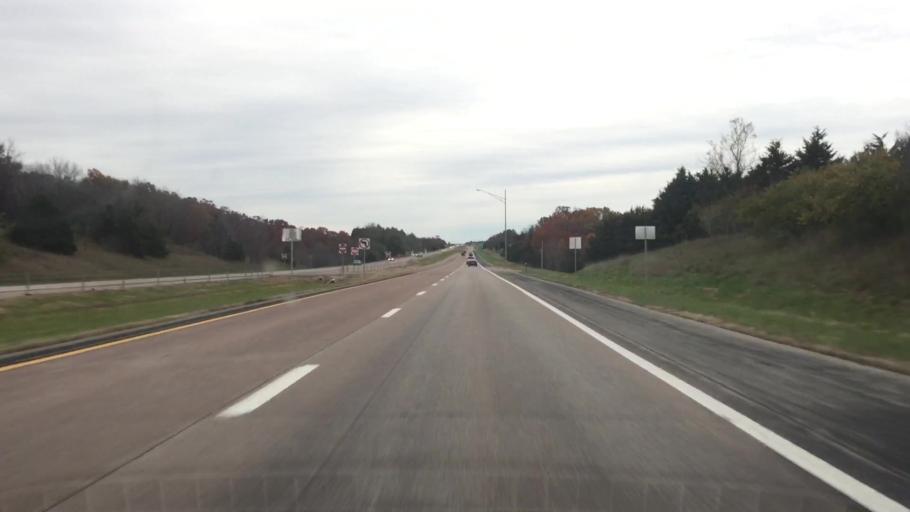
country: US
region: Missouri
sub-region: Boone County
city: Ashland
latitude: 38.7489
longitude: -92.2532
